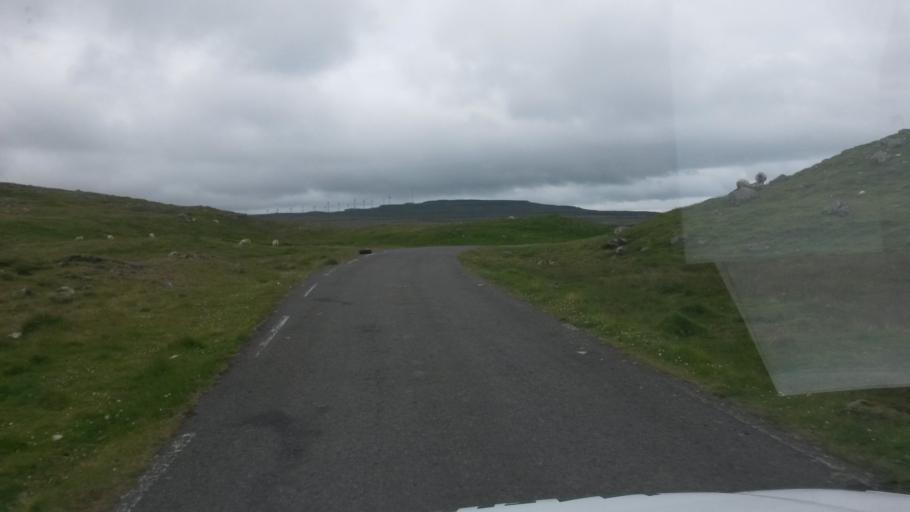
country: FO
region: Streymoy
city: Argir
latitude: 61.9943
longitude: -6.8478
